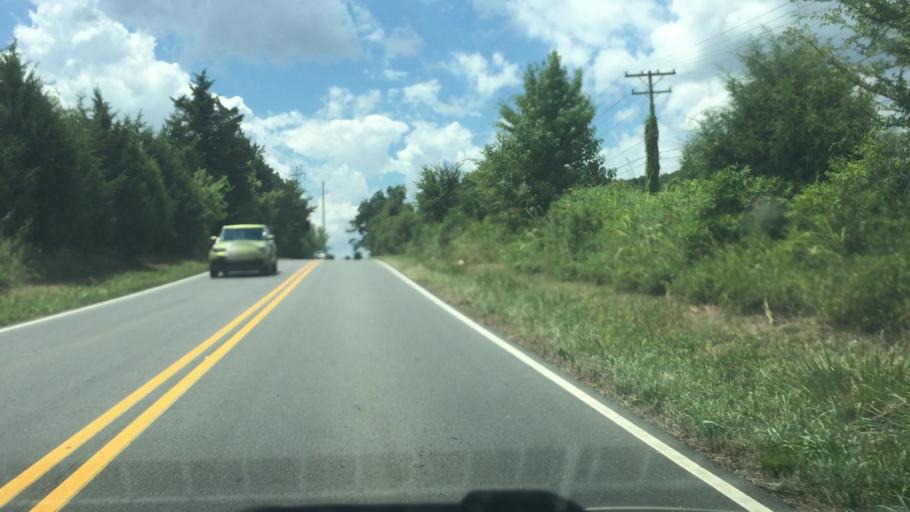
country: US
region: North Carolina
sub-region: Mecklenburg County
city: Huntersville
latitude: 35.4090
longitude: -80.7548
